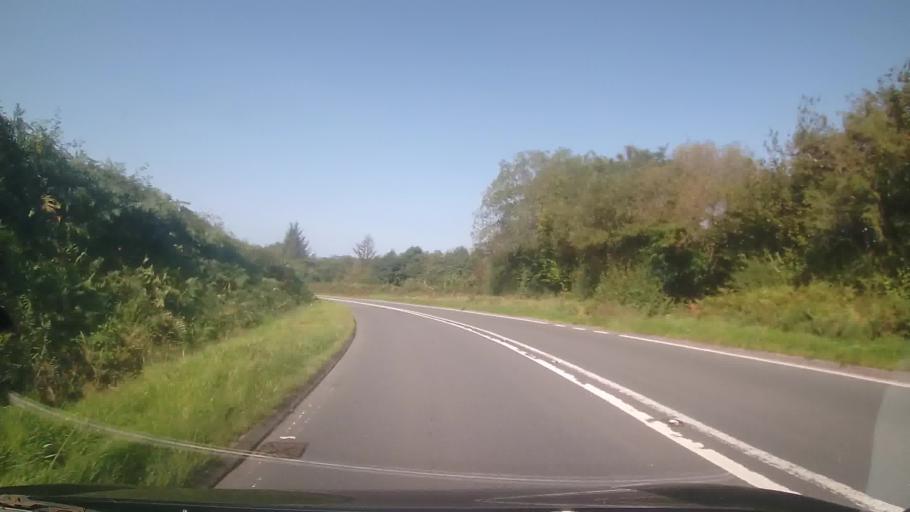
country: GB
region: Wales
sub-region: Sir Powys
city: Builth Wells
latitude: 52.1423
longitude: -3.5729
